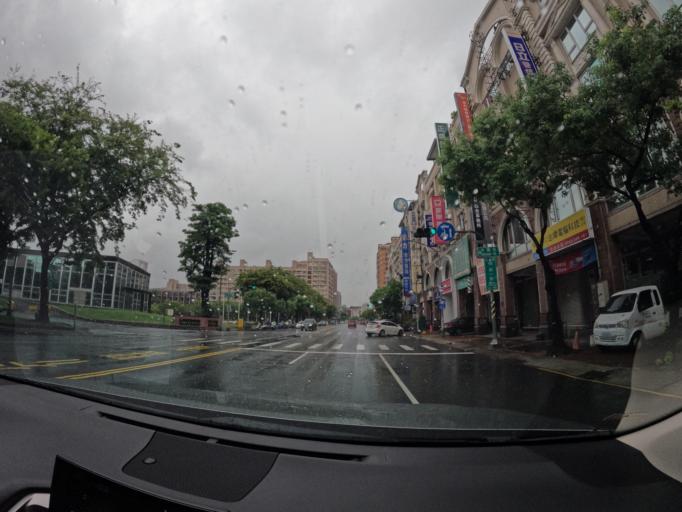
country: TW
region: Kaohsiung
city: Kaohsiung
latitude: 22.6597
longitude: 120.3252
